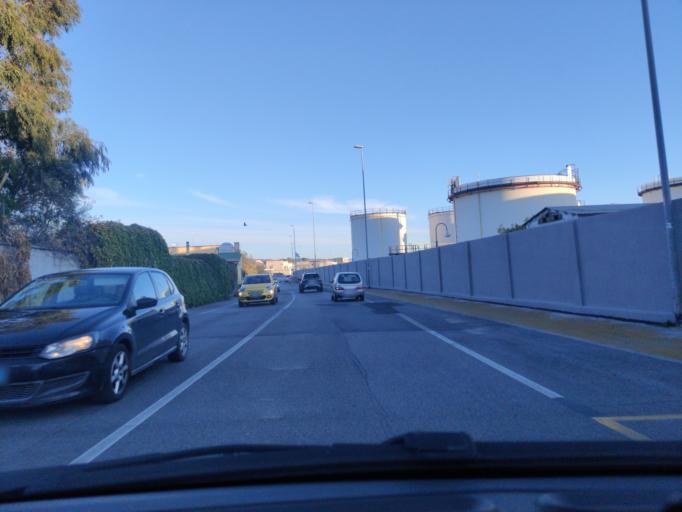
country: IT
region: Latium
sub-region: Citta metropolitana di Roma Capitale
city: Civitavecchia
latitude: 42.1080
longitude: 11.7796
